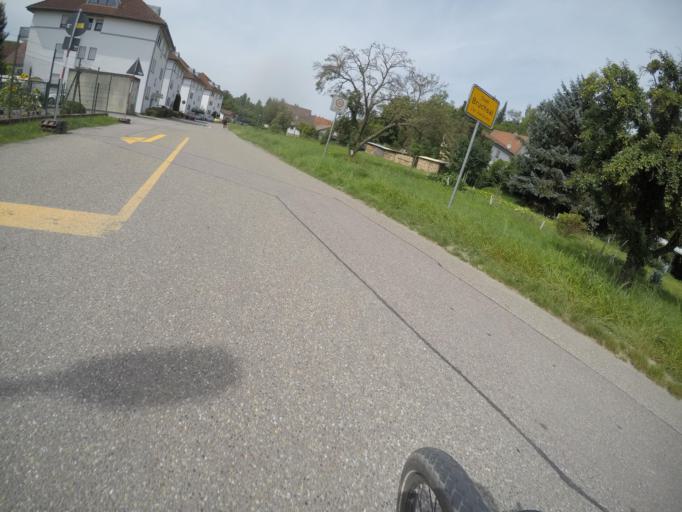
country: DE
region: Baden-Wuerttemberg
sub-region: Karlsruhe Region
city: Bruchsal
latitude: 49.1175
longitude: 8.6204
